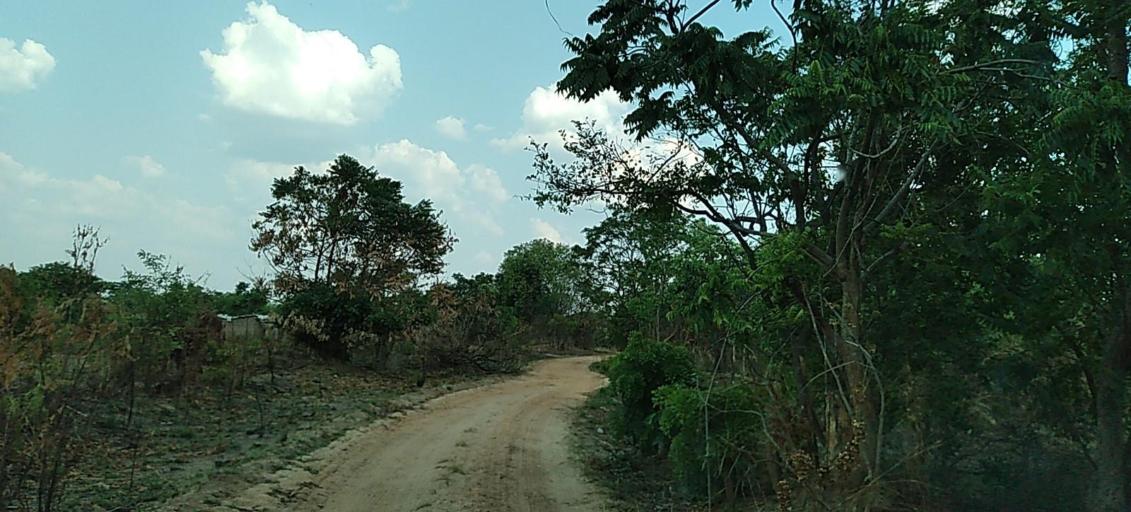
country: ZM
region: Copperbelt
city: Luanshya
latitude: -13.1573
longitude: 28.3314
